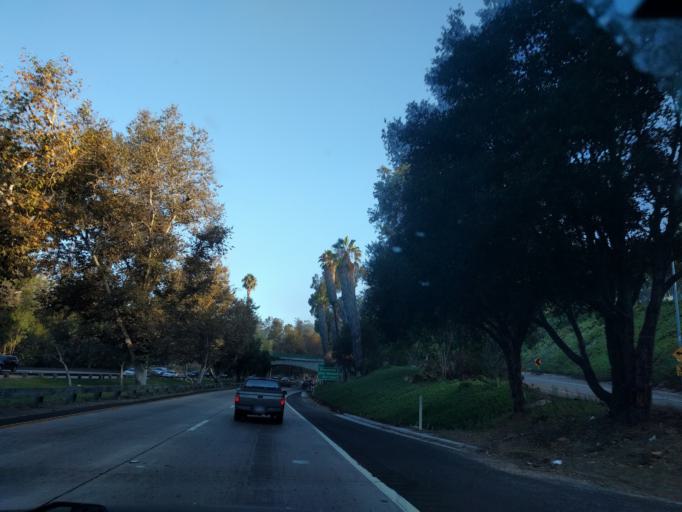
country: US
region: California
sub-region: San Diego County
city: San Diego
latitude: 32.7330
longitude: -117.1551
